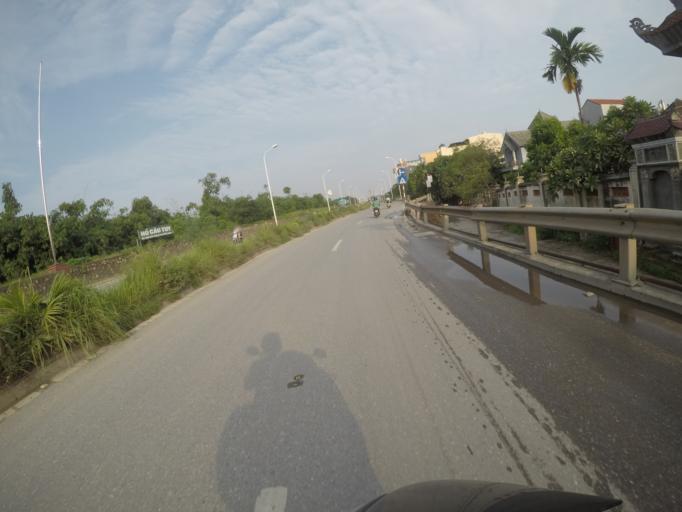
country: VN
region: Ha Noi
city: Tay Ho
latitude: 21.0909
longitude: 105.7877
